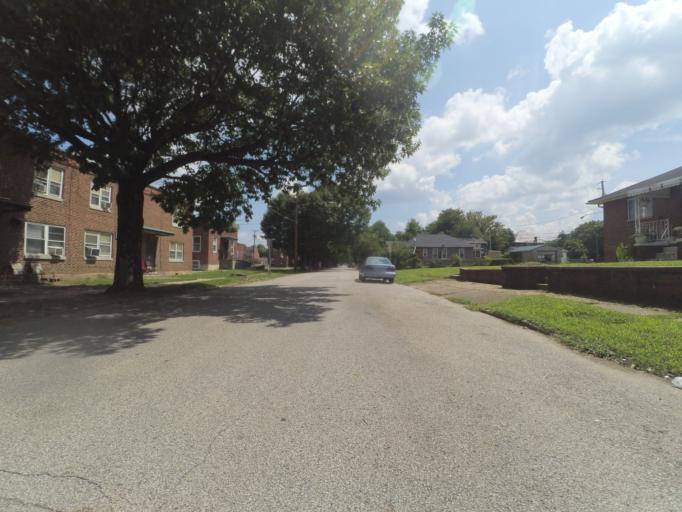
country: US
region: West Virginia
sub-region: Cabell County
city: Huntington
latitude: 38.4167
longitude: -82.4290
